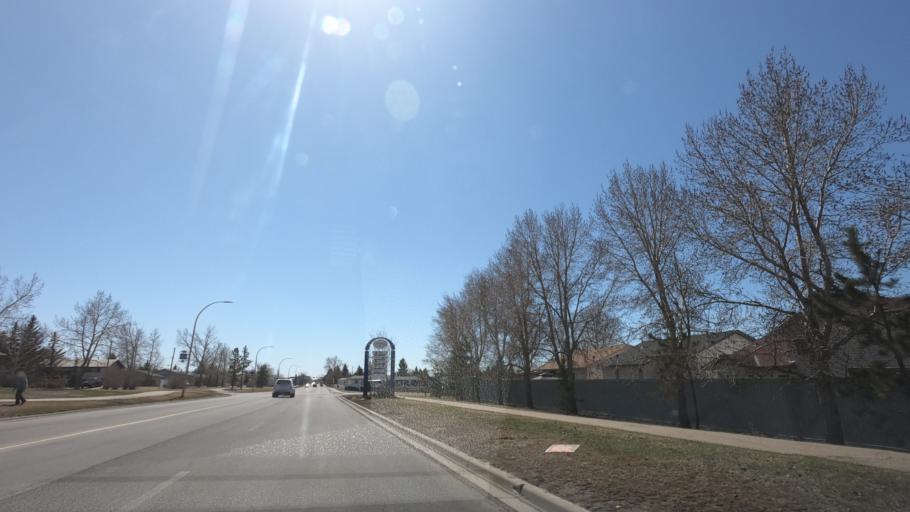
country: CA
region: Alberta
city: Airdrie
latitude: 51.2989
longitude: -114.0135
